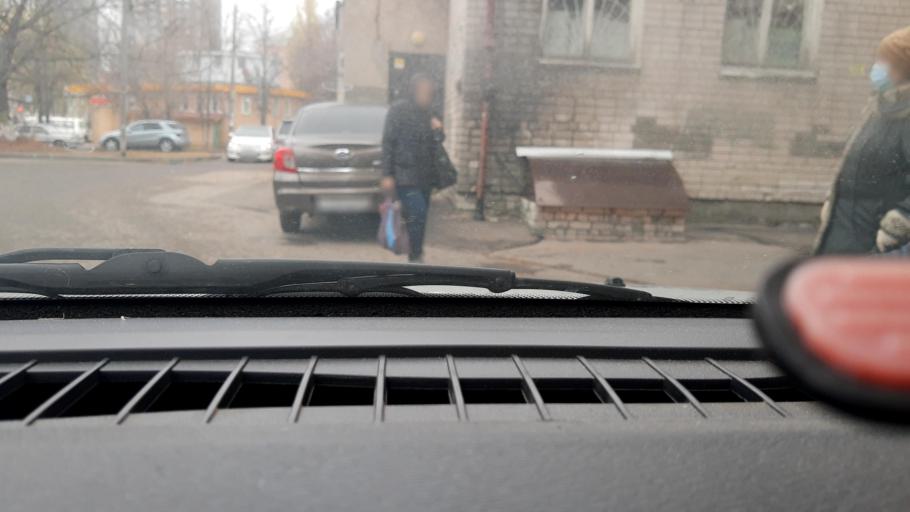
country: RU
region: Nizjnij Novgorod
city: Gorbatovka
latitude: 56.2617
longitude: 43.8821
